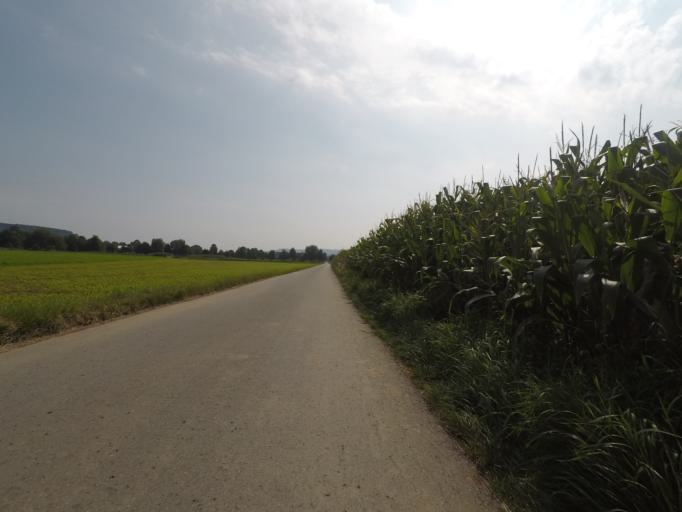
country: DE
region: Baden-Wuerttemberg
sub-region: Regierungsbezirk Stuttgart
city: Winterbach
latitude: 48.8018
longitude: 9.4639
